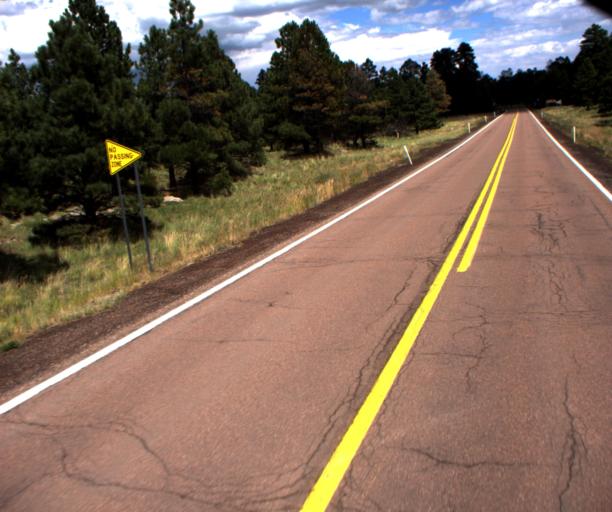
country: US
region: Arizona
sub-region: Apache County
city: Eagar
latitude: 34.0567
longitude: -109.5035
